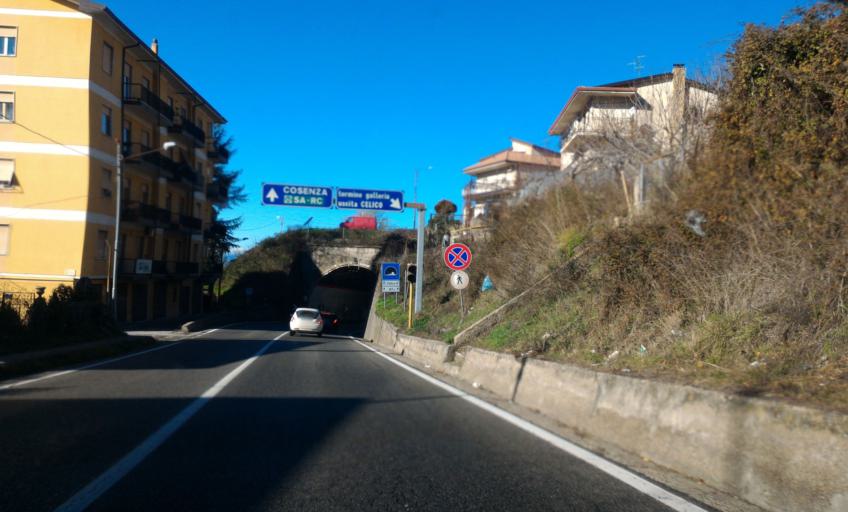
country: IT
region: Calabria
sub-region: Provincia di Cosenza
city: Celico
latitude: 39.3077
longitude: 16.3414
